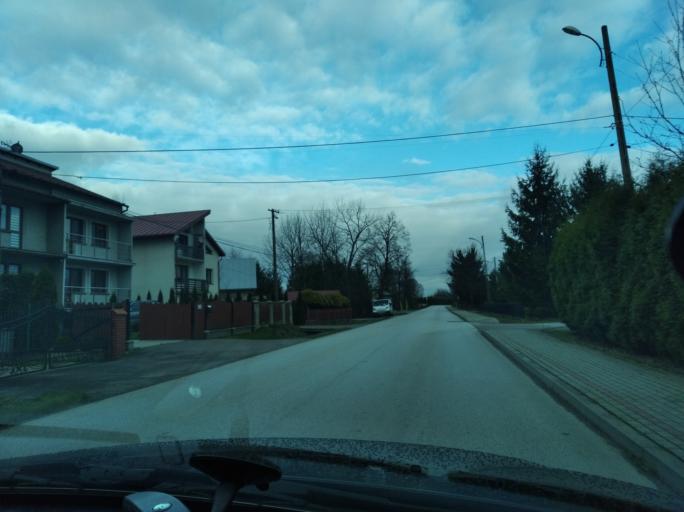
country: PL
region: Subcarpathian Voivodeship
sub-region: Powiat lancucki
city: Gluchow
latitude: 50.0976
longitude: 22.2620
